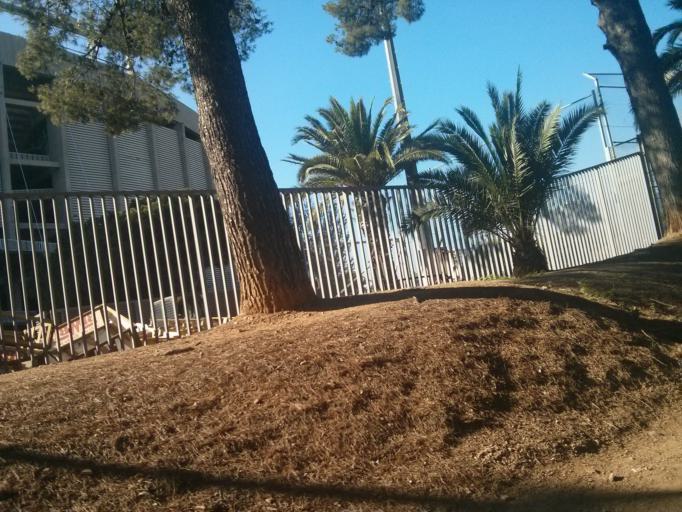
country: ES
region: Catalonia
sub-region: Provincia de Barcelona
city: les Corts
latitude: 41.3820
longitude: 2.1243
